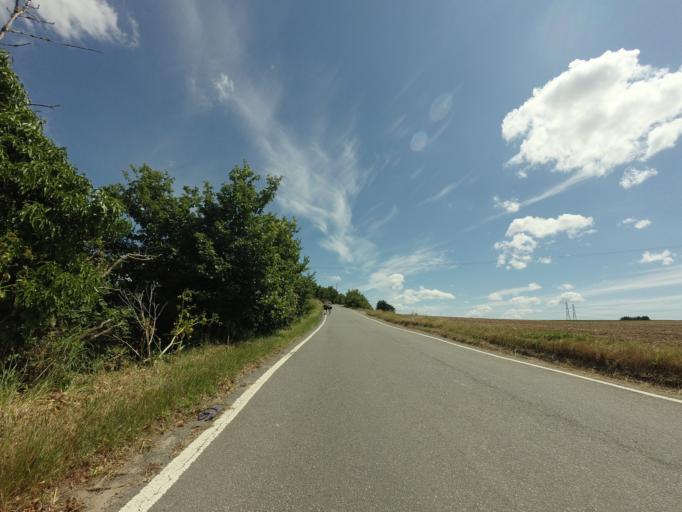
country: GB
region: England
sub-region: Medway
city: High Halstow
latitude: 51.4513
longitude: 0.5486
